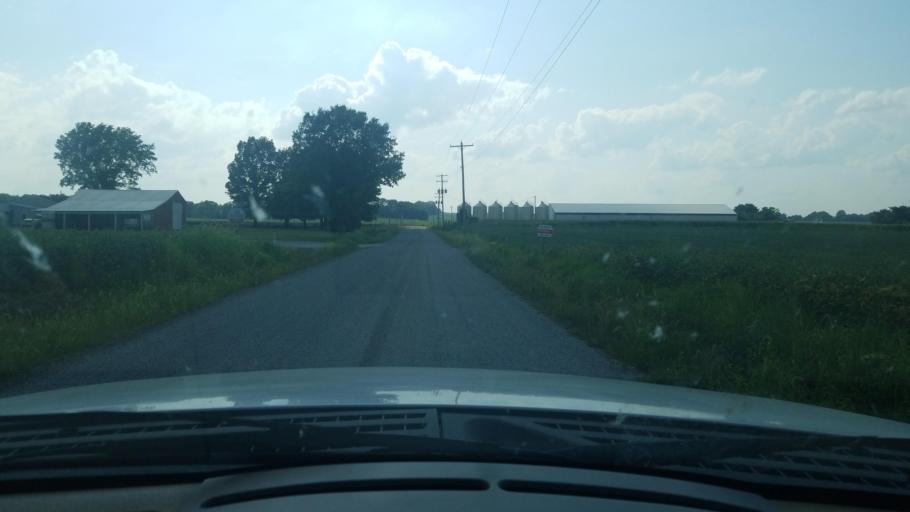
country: US
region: Illinois
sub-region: Saline County
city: Eldorado
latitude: 37.8344
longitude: -88.4484
